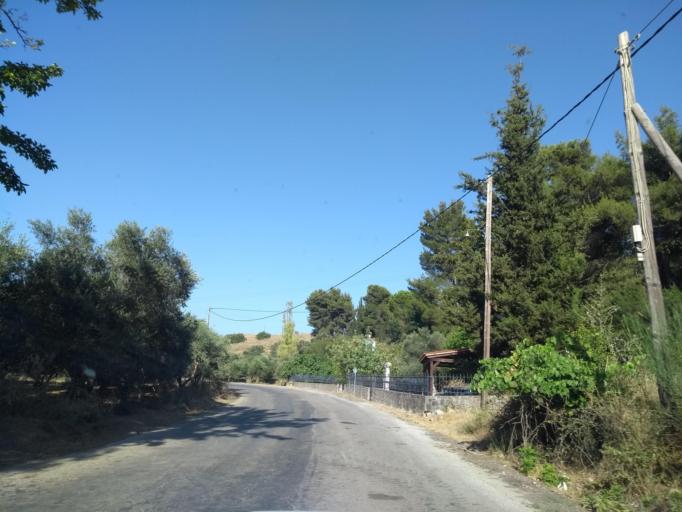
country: GR
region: Crete
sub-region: Nomos Chanias
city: Georgioupolis
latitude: 35.3657
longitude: 24.2260
